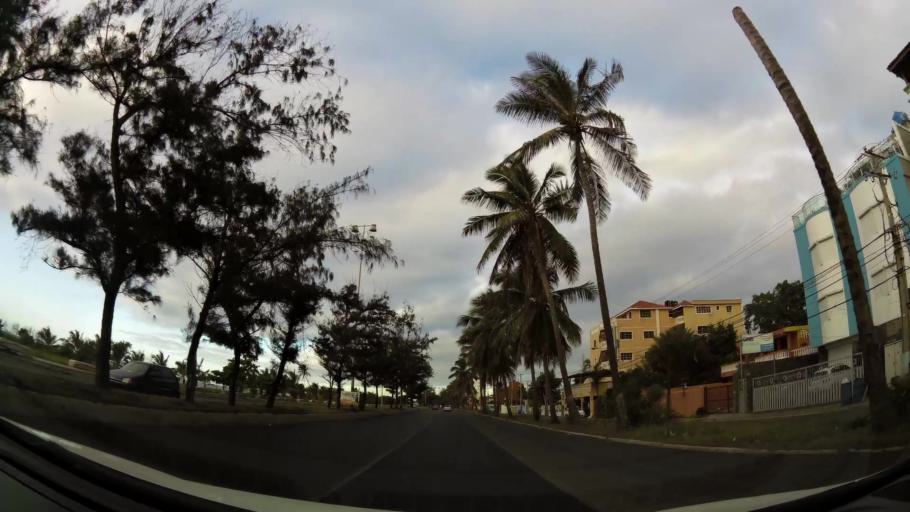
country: DO
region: Nacional
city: Bella Vista
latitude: 18.4308
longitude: -69.9600
